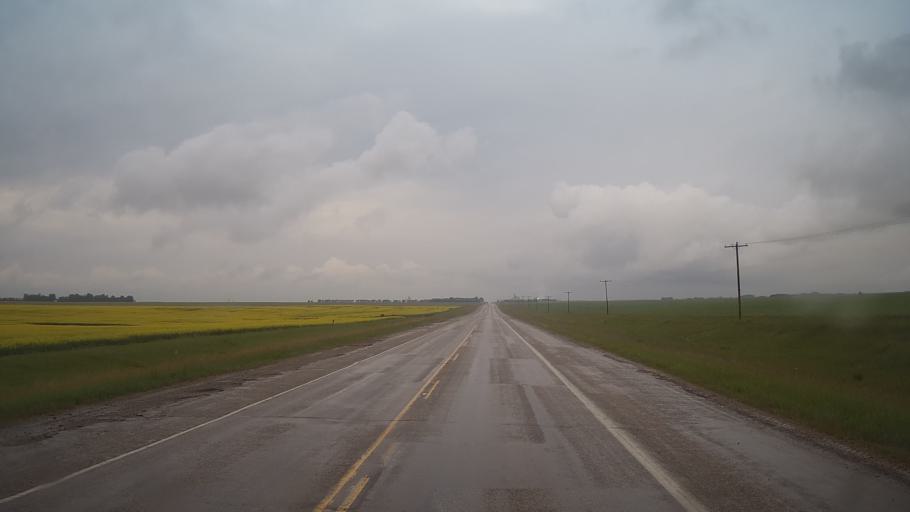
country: CA
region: Saskatchewan
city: Unity
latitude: 52.4350
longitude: -109.0513
